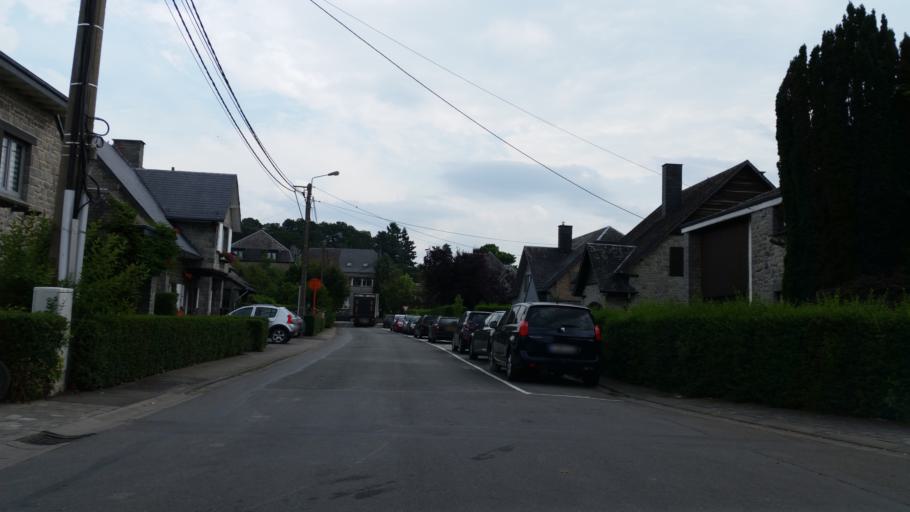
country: BE
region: Wallonia
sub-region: Province de Namur
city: Rochefort
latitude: 50.1270
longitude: 5.1876
